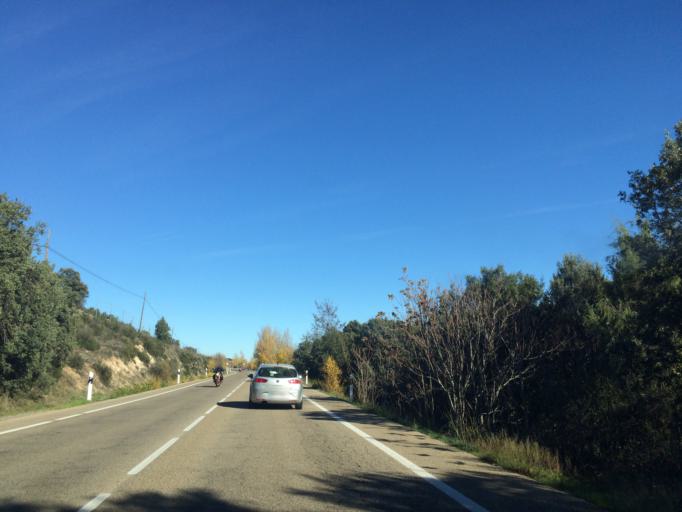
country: ES
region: Madrid
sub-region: Provincia de Madrid
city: Boalo
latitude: 40.7162
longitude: -3.8901
